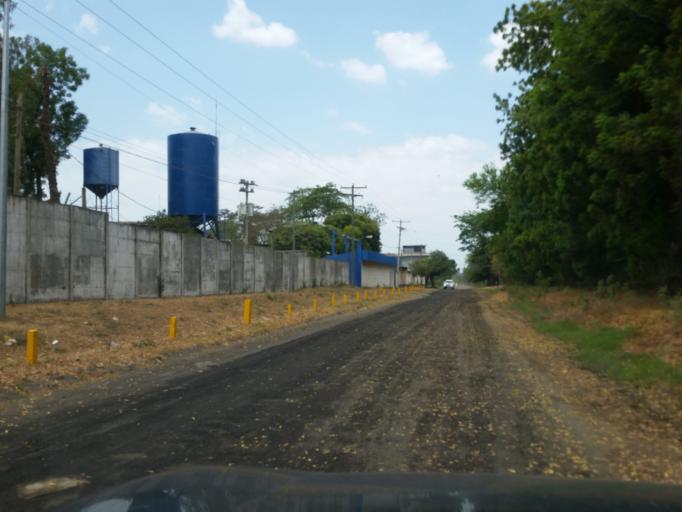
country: NI
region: Managua
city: Managua
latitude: 12.1286
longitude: -86.1647
